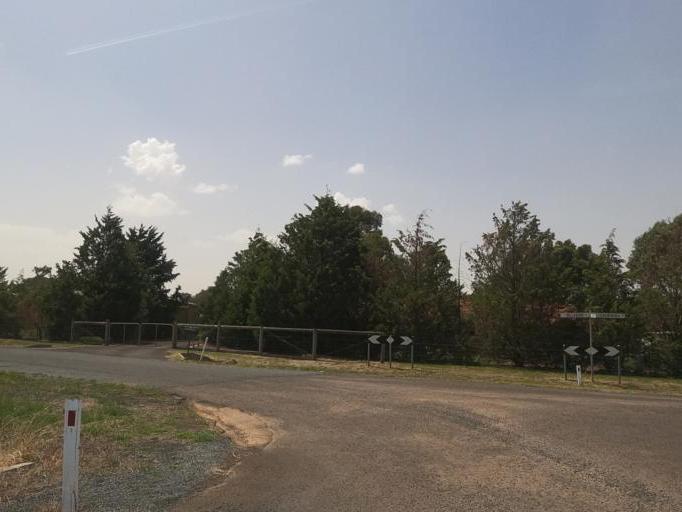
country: AU
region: Victoria
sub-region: Hume
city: Craigieburn
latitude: -37.5581
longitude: 144.8915
